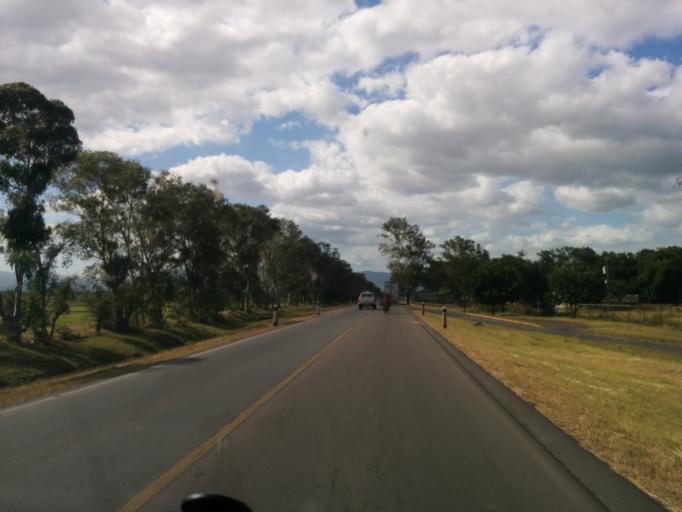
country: NI
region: Matagalpa
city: Ciudad Dario
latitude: 12.8636
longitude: -86.1123
